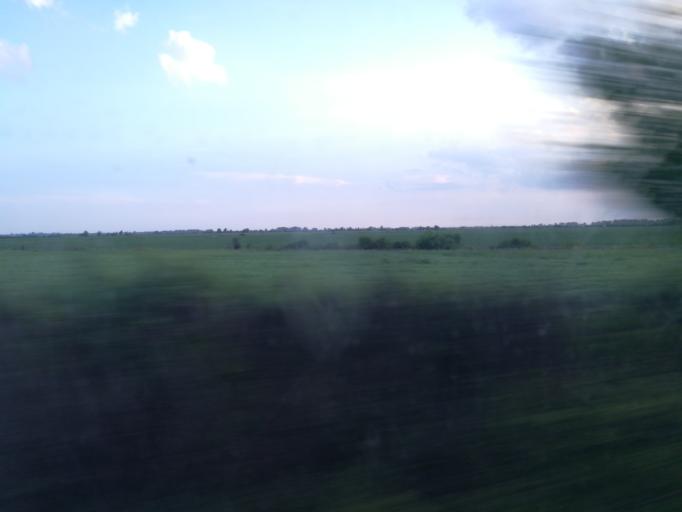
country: RO
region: Dambovita
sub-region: Comuna Contesti
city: Balteni
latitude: 44.6502
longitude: 25.6850
